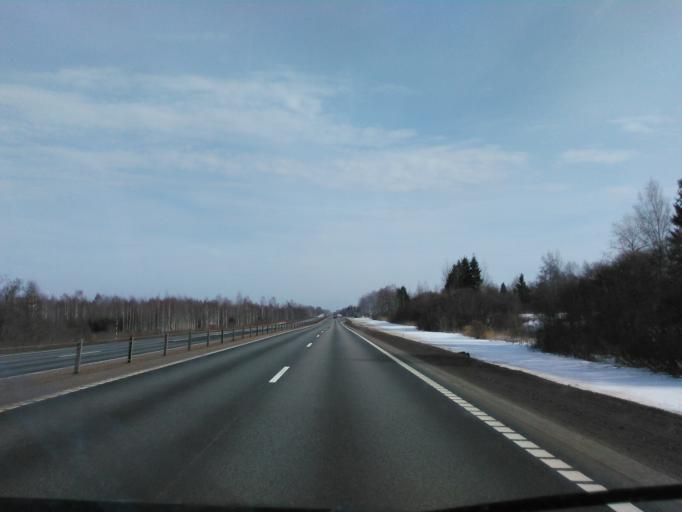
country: BY
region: Vitebsk
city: Dubrowna
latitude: 54.6894
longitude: 30.8973
